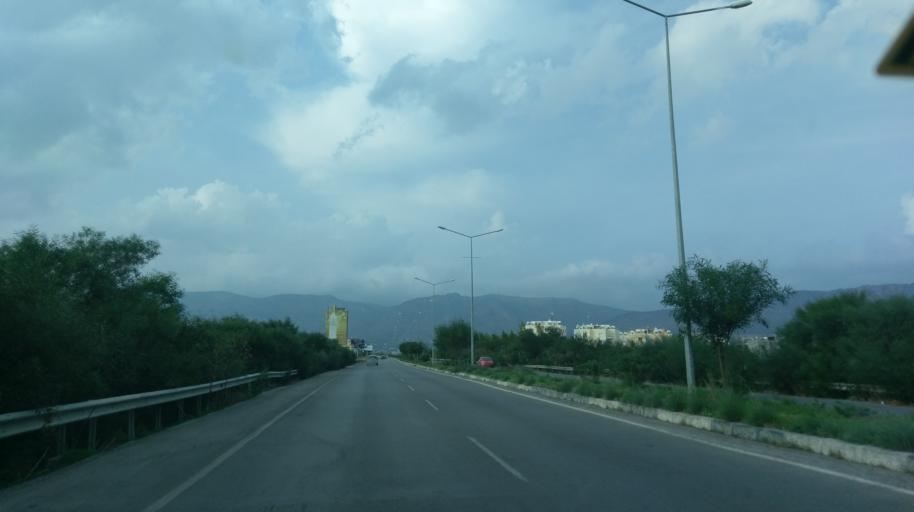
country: CY
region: Keryneia
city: Kyrenia
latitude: 35.2562
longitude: 33.2997
